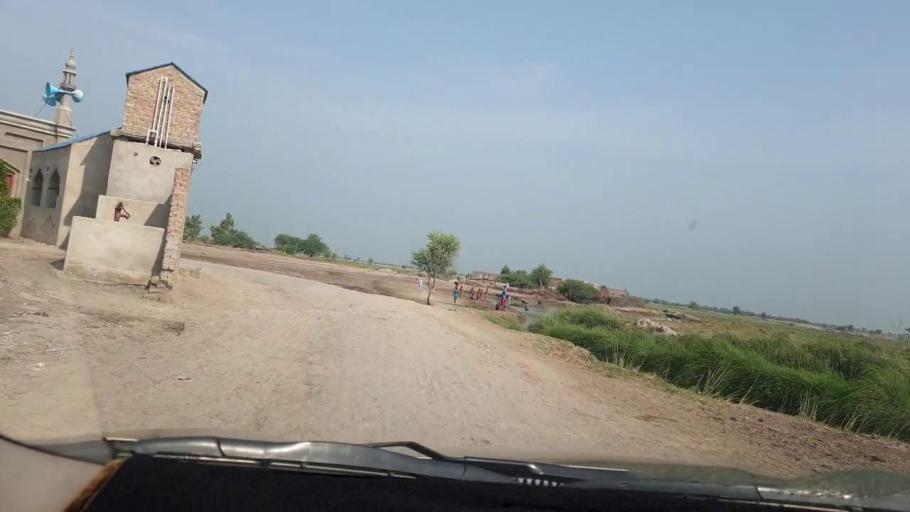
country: PK
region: Sindh
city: Goth Garelo
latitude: 27.4483
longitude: 68.0333
